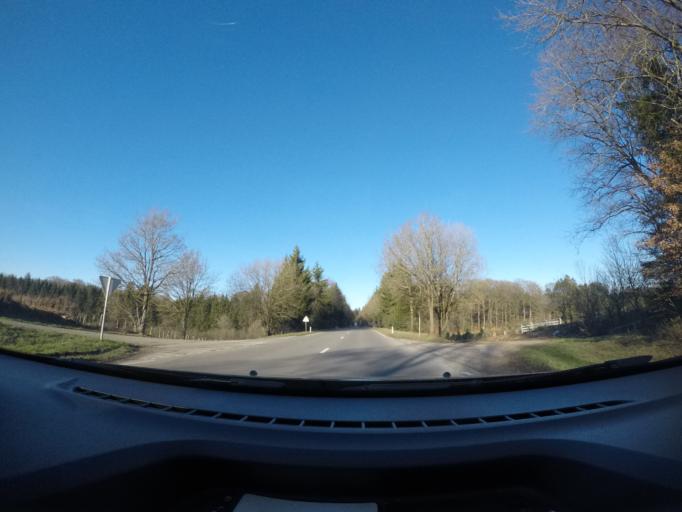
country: BE
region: Wallonia
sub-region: Province du Luxembourg
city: Bertrix
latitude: 49.8659
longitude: 5.2743
